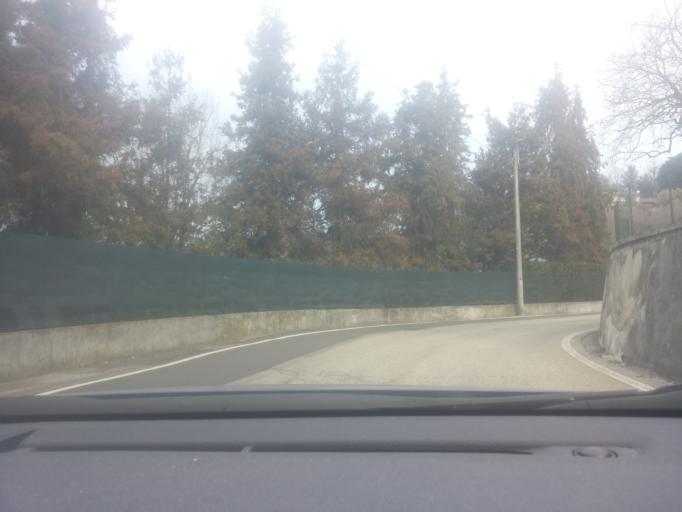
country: IT
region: Piedmont
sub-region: Provincia di Torino
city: Revigliasco
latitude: 45.0534
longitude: 7.7254
